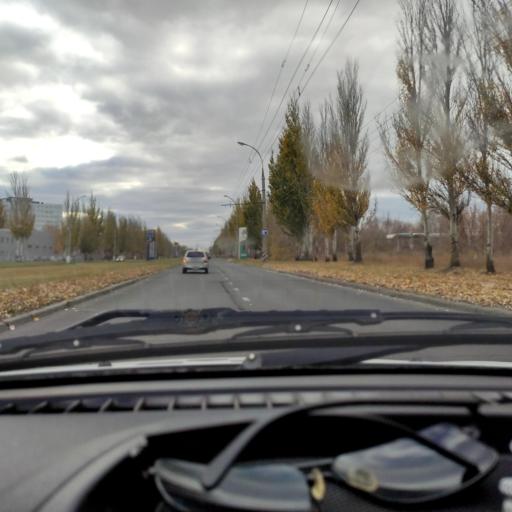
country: RU
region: Samara
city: Tol'yatti
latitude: 53.5509
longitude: 49.2695
